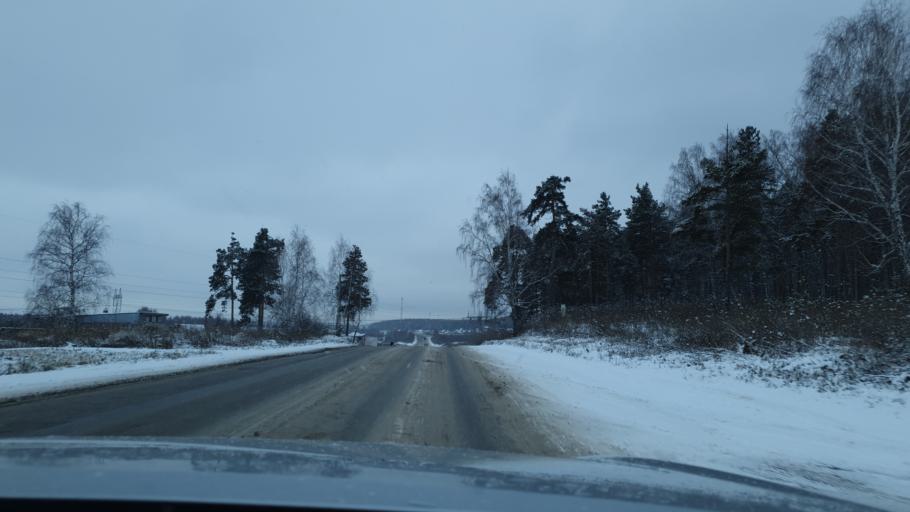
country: RU
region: Sverdlovsk
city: Istok
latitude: 56.7777
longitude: 60.7396
